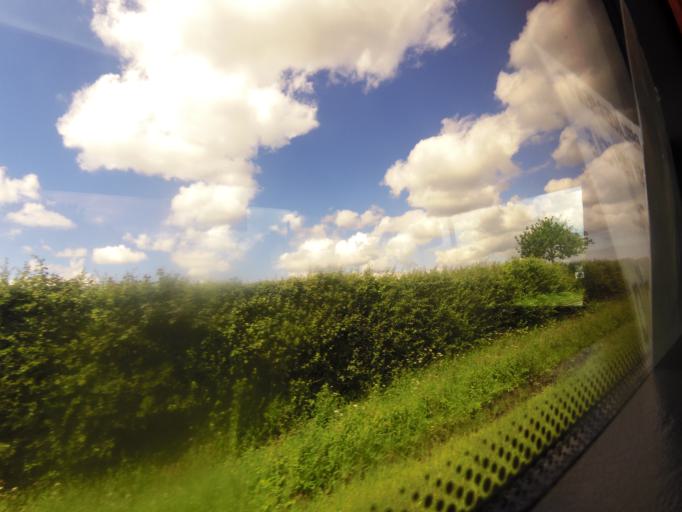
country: GB
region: England
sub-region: Norfolk
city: Aylsham
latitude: 52.8255
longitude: 1.2737
